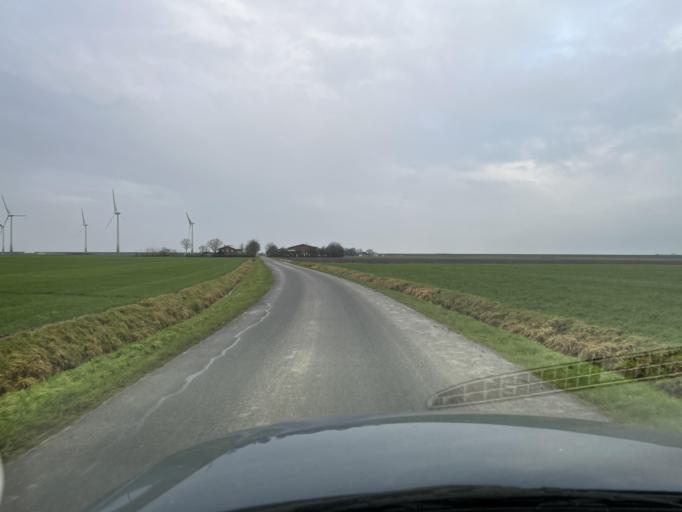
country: DE
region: Schleswig-Holstein
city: Hillgroven
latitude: 54.2196
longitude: 8.8716
